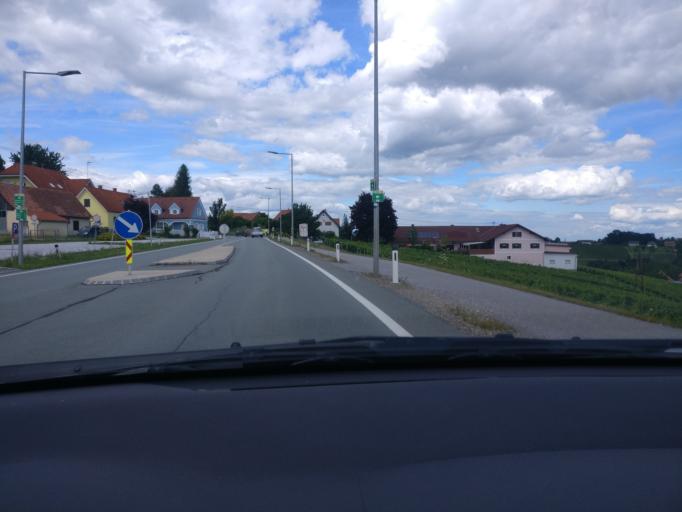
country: AT
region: Styria
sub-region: Politischer Bezirk Weiz
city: Nitscha
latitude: 47.1325
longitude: 15.7300
